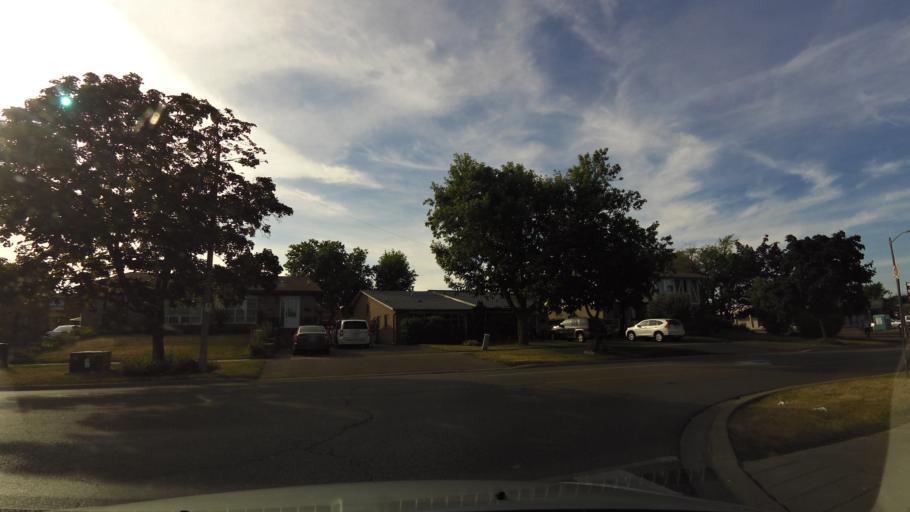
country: CA
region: Ontario
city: Brampton
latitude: 43.6885
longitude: -79.7429
